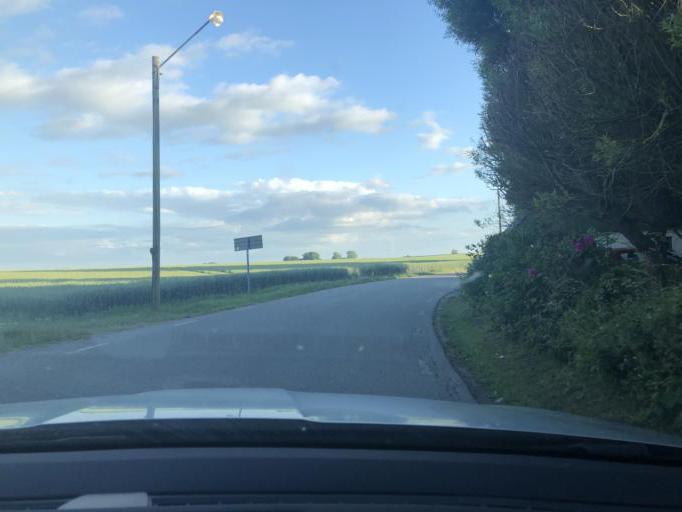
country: SE
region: Skane
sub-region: Simrishamns Kommun
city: Simrishamn
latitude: 55.4964
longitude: 14.2030
